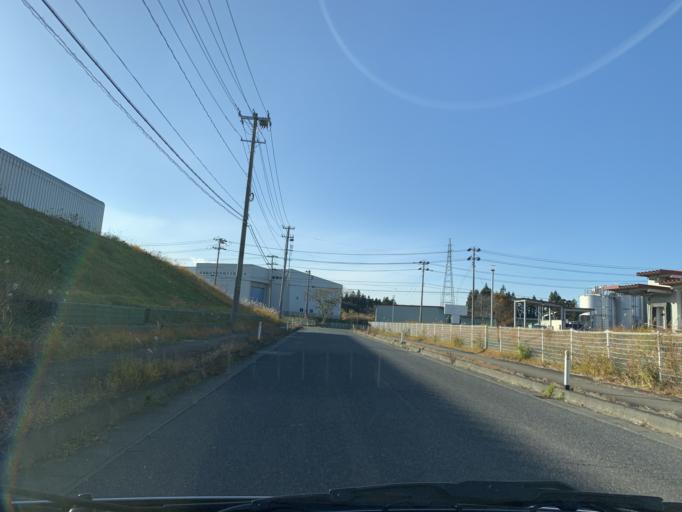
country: JP
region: Iwate
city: Kitakami
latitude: 39.2473
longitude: 141.0930
